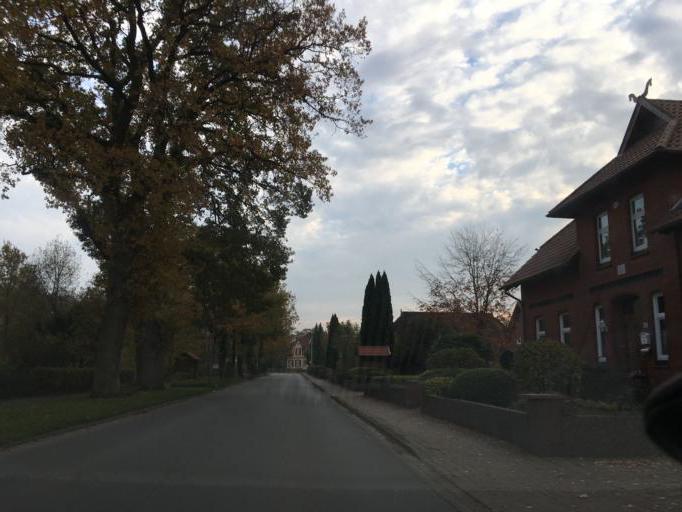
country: DE
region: Lower Saxony
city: Wietzendorf
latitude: 52.9163
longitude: 9.9766
